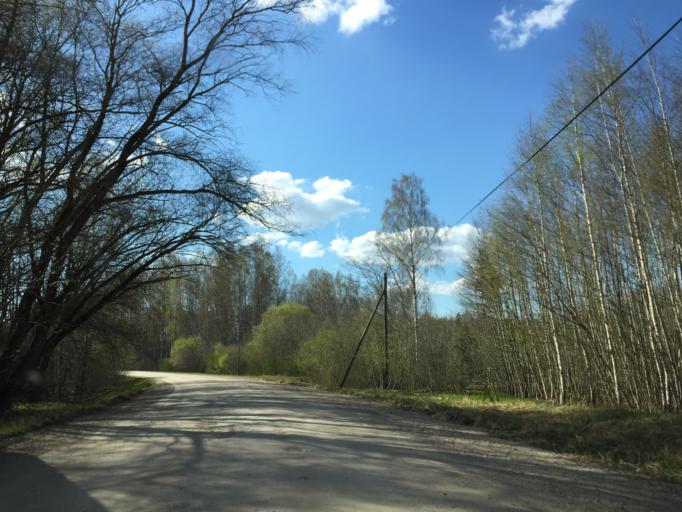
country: LV
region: Seja
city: Loja
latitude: 57.3457
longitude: 24.5942
